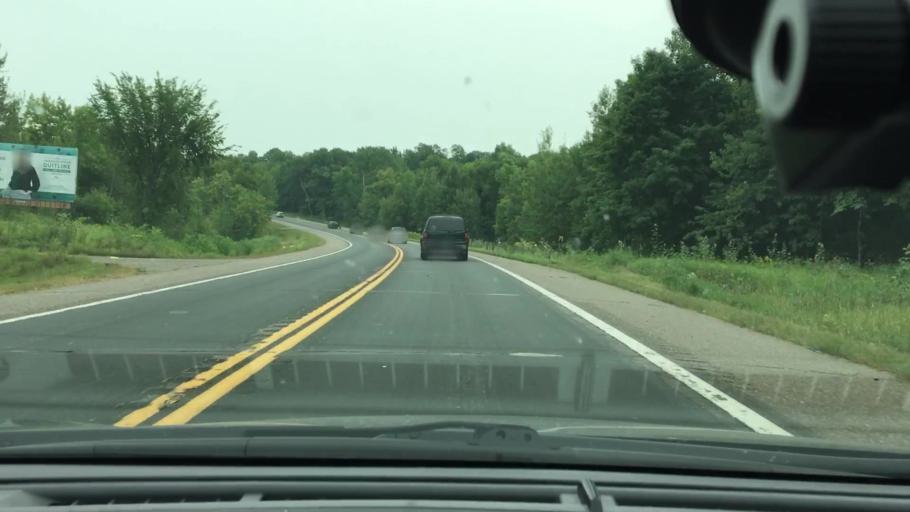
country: US
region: Minnesota
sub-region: Mille Lacs County
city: Vineland
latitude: 46.2039
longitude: -93.7824
